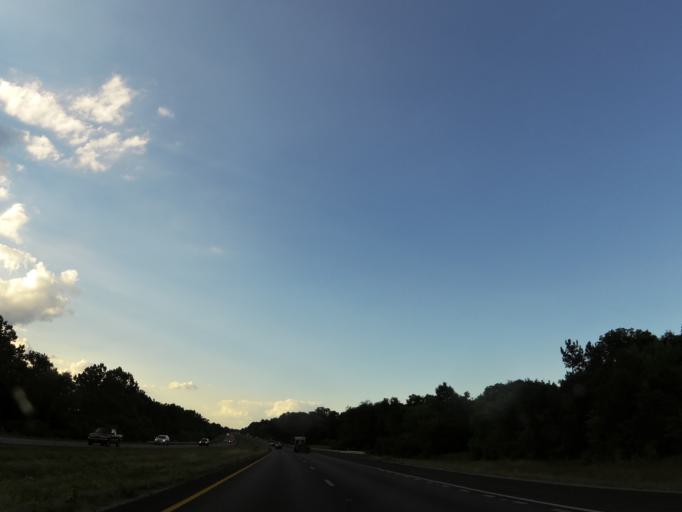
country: US
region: Tennessee
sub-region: Williamson County
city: Thompson's Station
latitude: 35.7624
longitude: -86.8654
